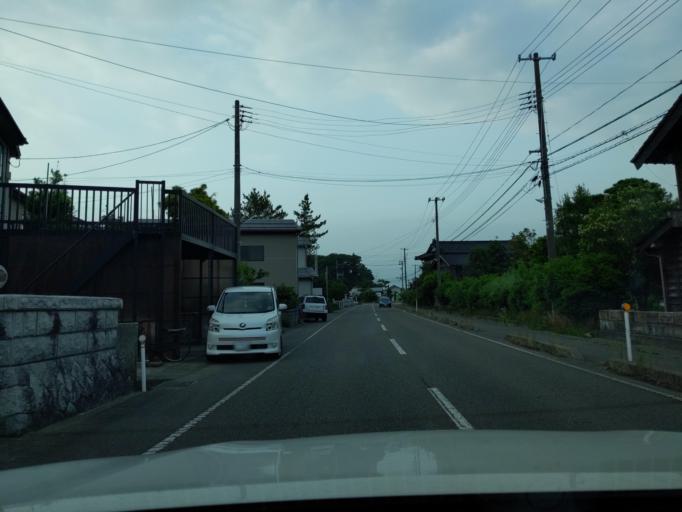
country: JP
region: Niigata
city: Kashiwazaki
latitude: 37.4193
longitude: 138.6155
